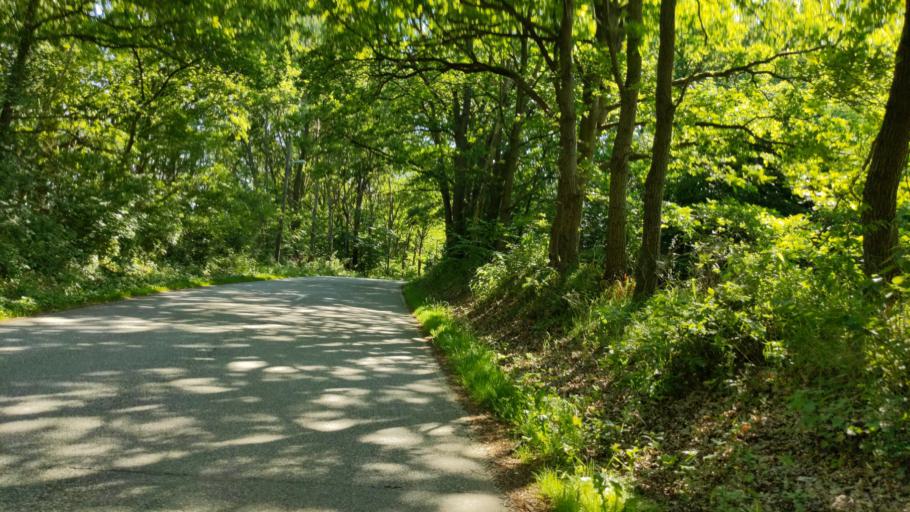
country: DE
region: Schleswig-Holstein
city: Gross Gronau
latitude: 53.8000
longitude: 10.7219
